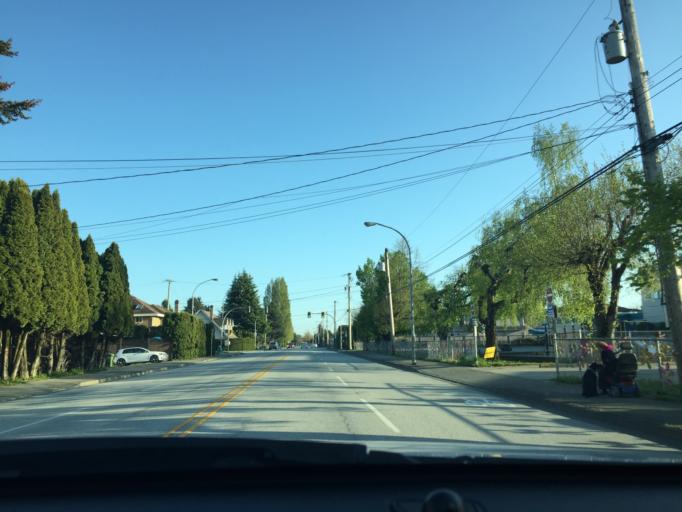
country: CA
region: British Columbia
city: Richmond
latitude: 49.1529
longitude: -123.1254
